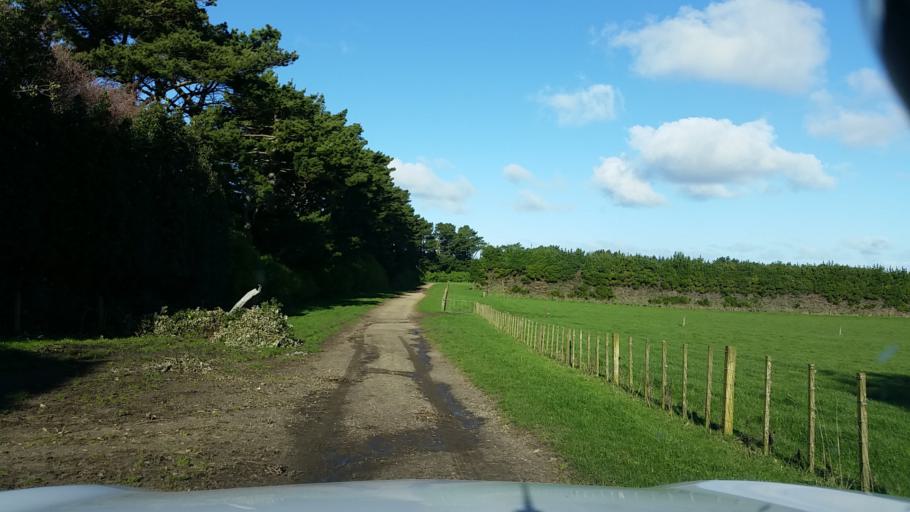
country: NZ
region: Taranaki
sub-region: South Taranaki District
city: Patea
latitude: -39.7382
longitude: 174.5416
